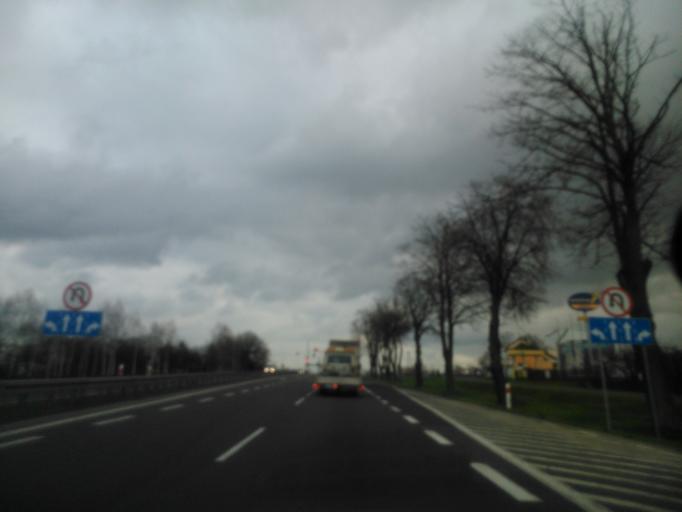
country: PL
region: Masovian Voivodeship
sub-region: Powiat plonski
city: Plonsk
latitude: 52.6012
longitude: 20.4084
